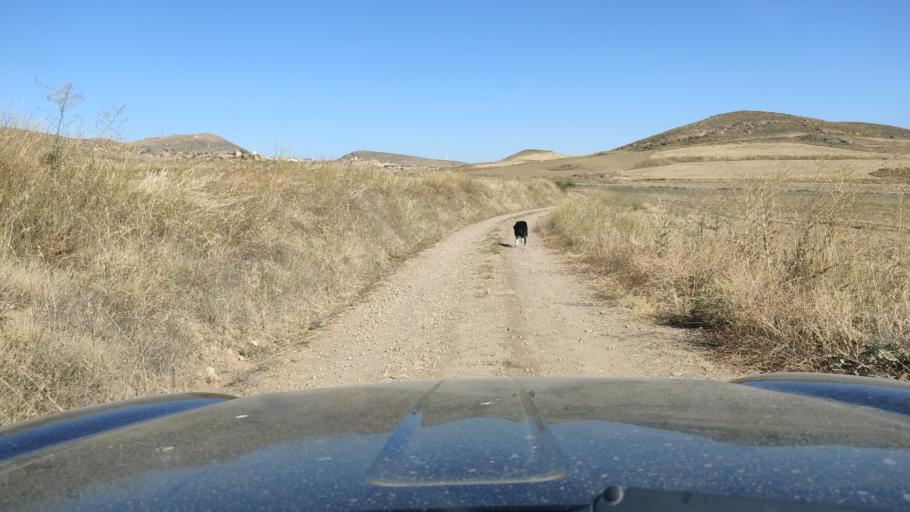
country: ES
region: Aragon
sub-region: Provincia de Teruel
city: Monforte de Moyuela
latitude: 41.0437
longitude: -1.0018
